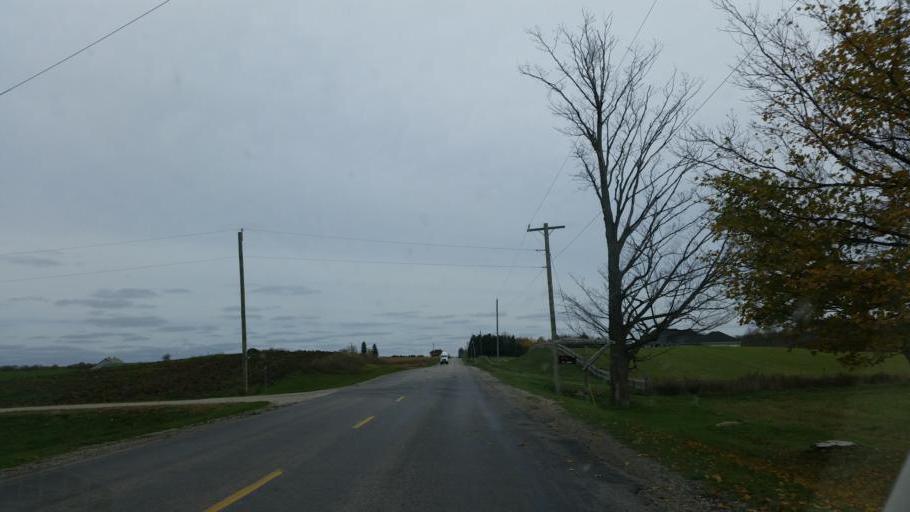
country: CA
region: Ontario
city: Wingham
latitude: 43.9955
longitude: -81.3230
